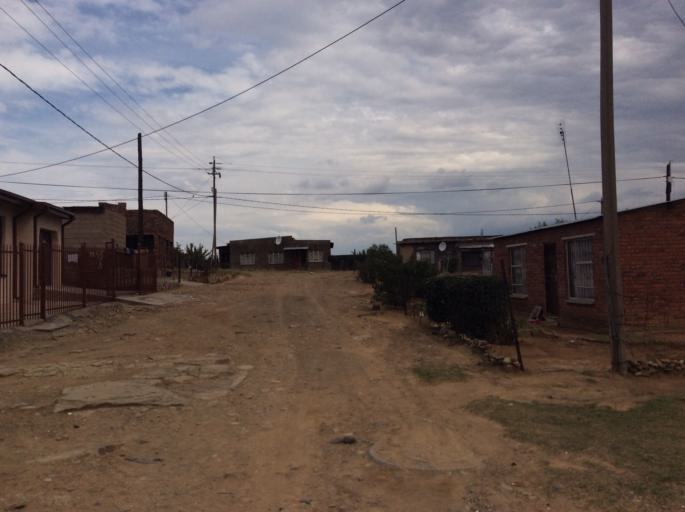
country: LS
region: Mafeteng
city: Mafeteng
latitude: -29.7223
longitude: 27.0304
